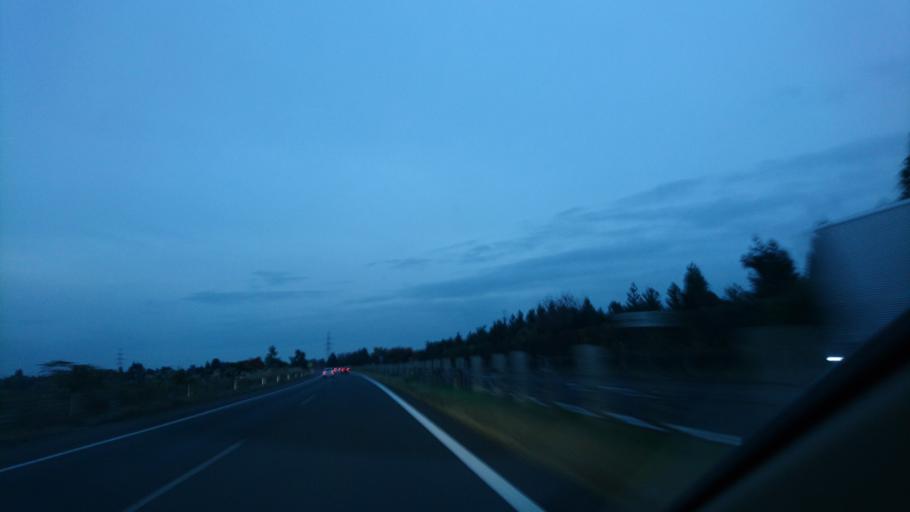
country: JP
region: Iwate
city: Morioka-shi
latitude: 39.5899
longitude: 141.1176
